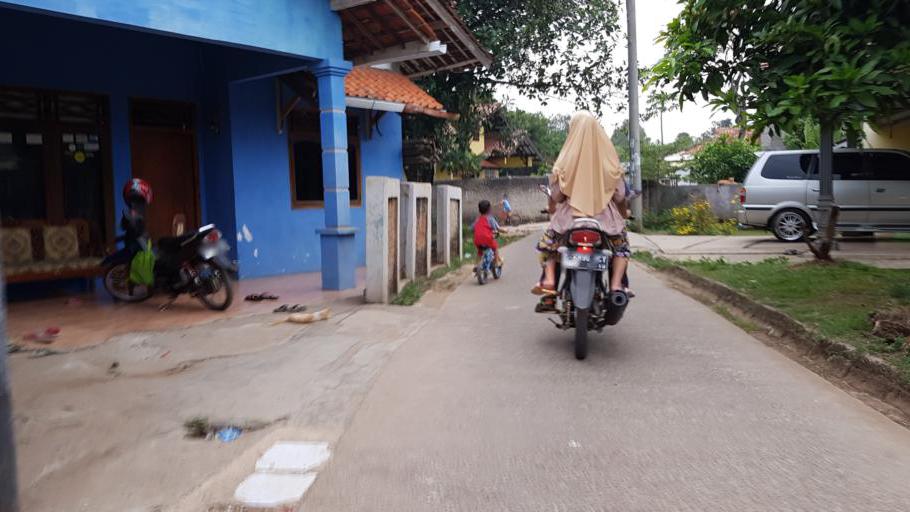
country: ID
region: West Java
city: Sawangan
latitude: -6.3982
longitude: 106.7684
